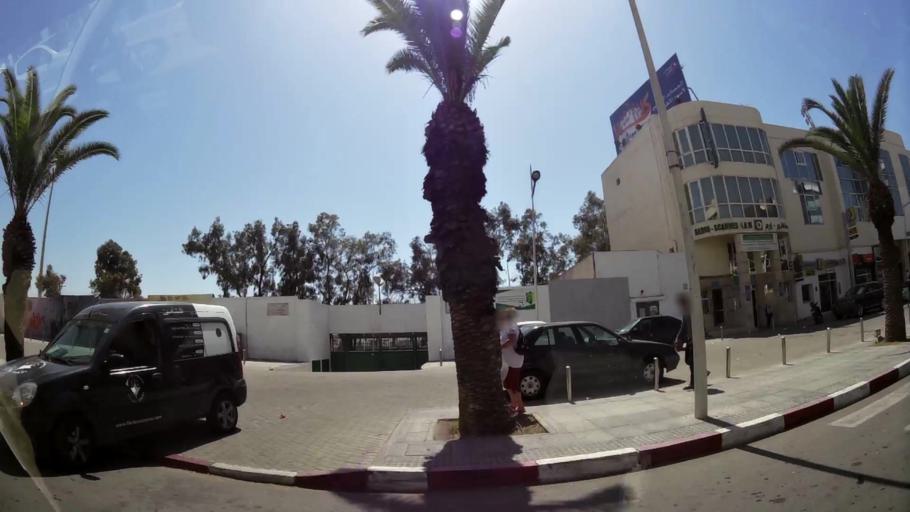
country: MA
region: Souss-Massa-Draa
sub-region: Agadir-Ida-ou-Tnan
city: Agadir
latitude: 30.4154
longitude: -9.5949
